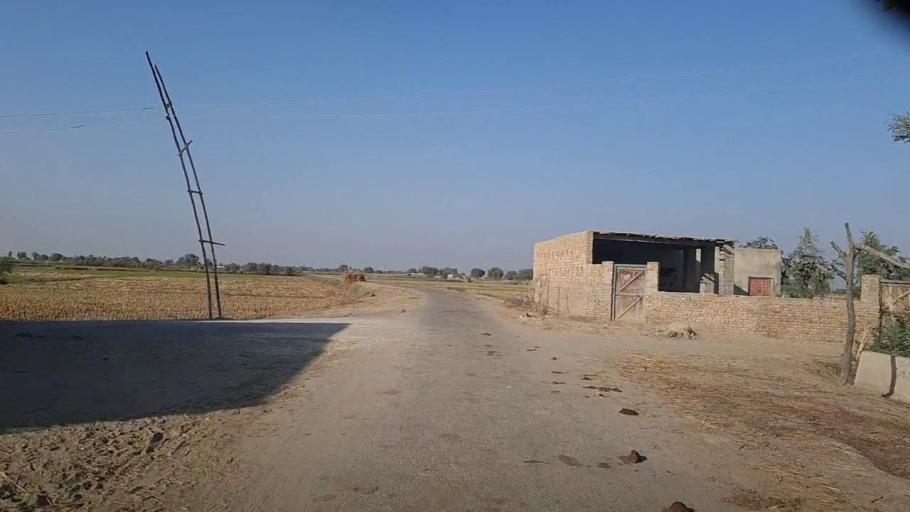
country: PK
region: Sindh
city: Tangwani
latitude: 28.2942
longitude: 68.9506
